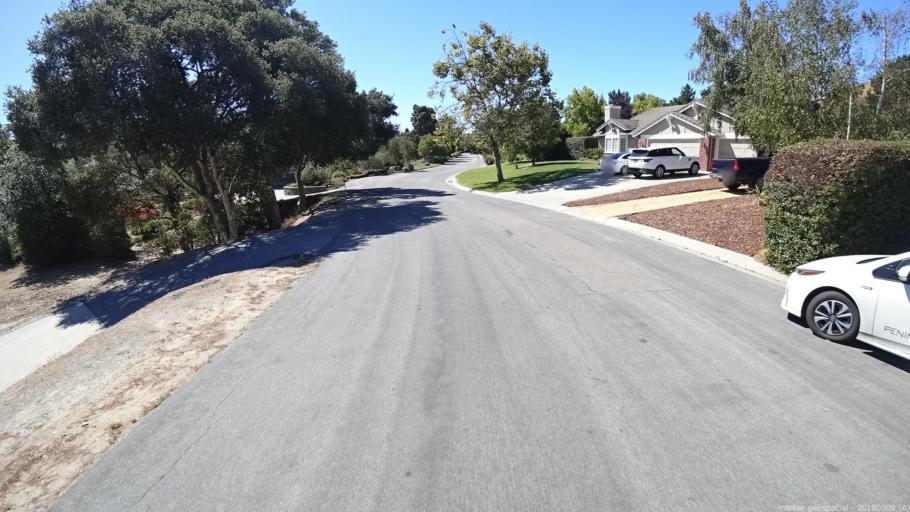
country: US
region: California
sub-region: Monterey County
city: Salinas
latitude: 36.6059
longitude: -121.7002
